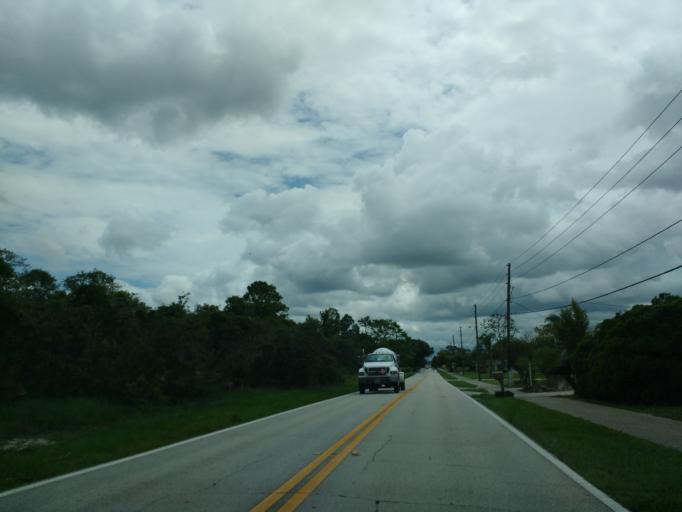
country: US
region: Florida
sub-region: Highlands County
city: Sebring
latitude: 27.4726
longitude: -81.4790
